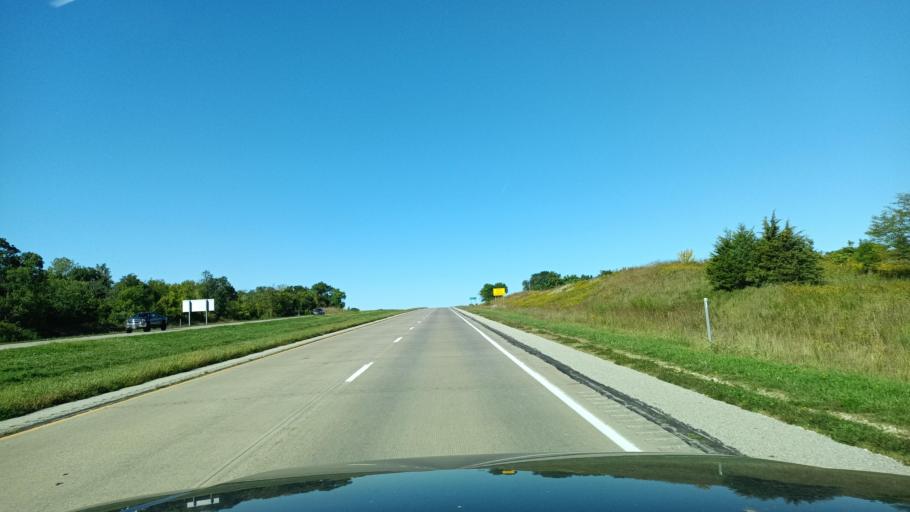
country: US
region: Iowa
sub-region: Lee County
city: Fort Madison
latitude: 40.6708
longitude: -91.2870
